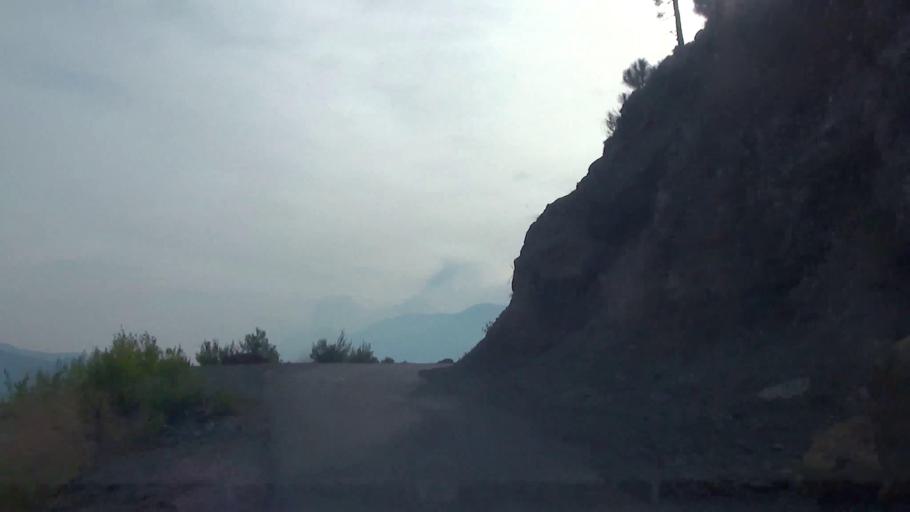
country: PK
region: Azad Kashmir
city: Muzaffarabad
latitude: 34.3656
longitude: 73.5032
